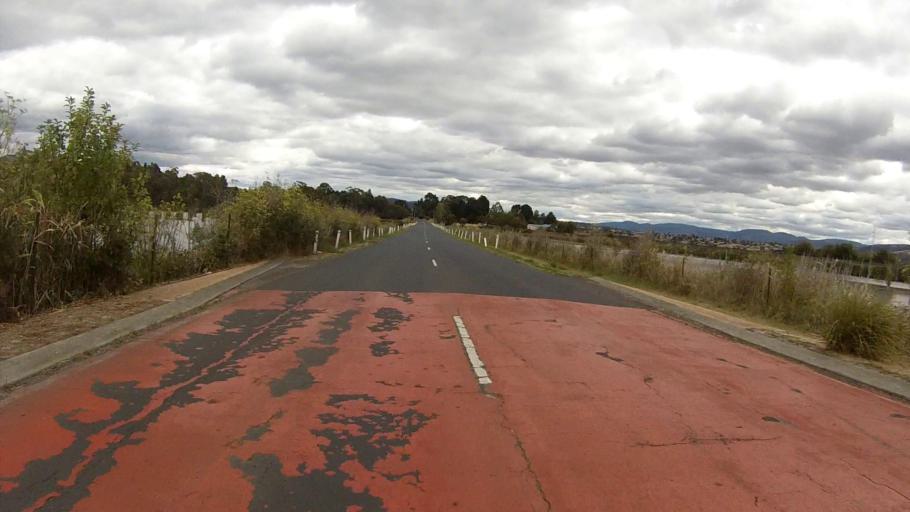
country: AU
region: Tasmania
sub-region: Glenorchy
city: Austins Ferry
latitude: -42.7655
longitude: 147.2430
